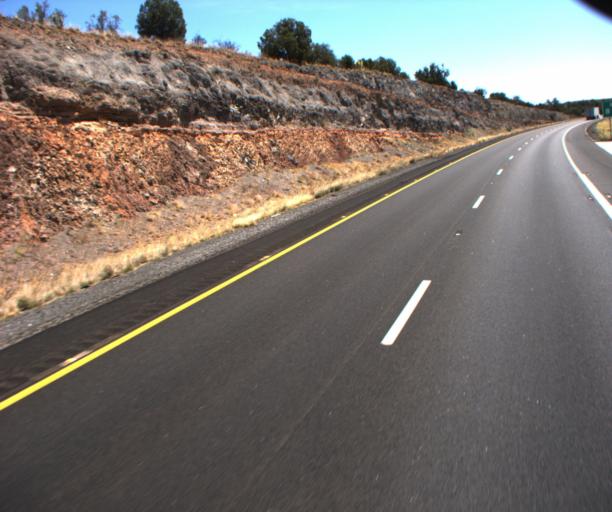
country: US
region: Arizona
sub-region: Mohave County
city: Peach Springs
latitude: 35.1898
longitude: -113.4417
